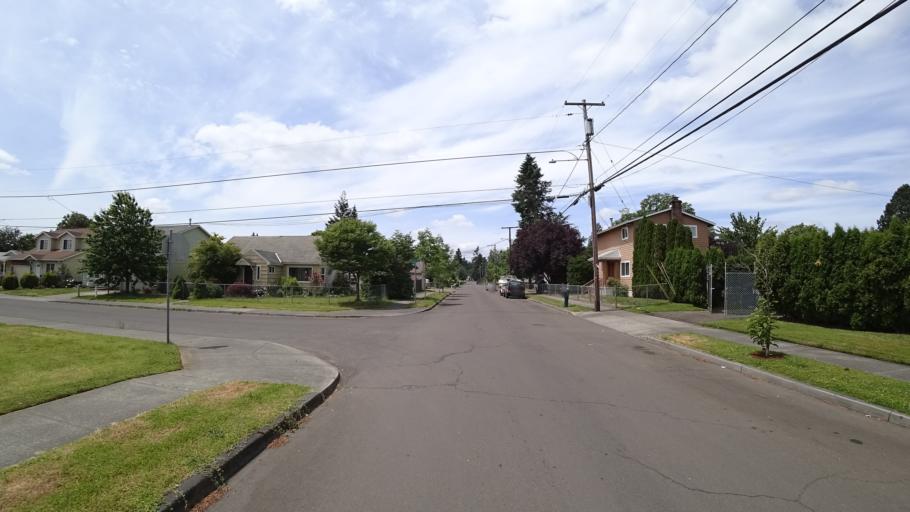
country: US
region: Oregon
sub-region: Multnomah County
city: Lents
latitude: 45.4641
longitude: -122.5954
